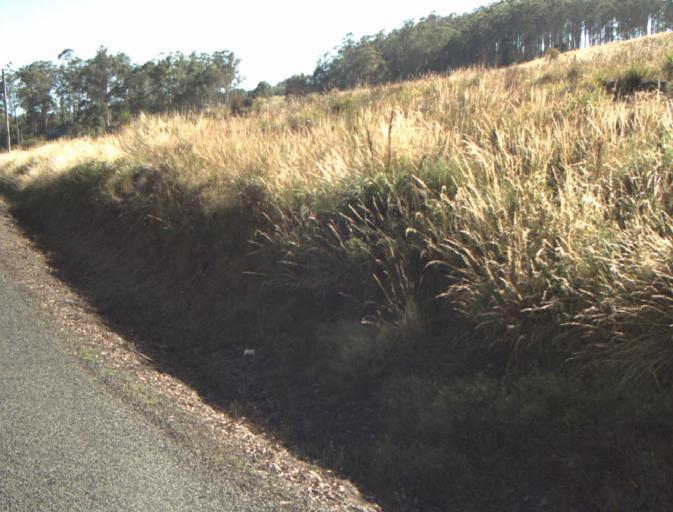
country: AU
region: Tasmania
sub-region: Launceston
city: Newstead
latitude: -41.3601
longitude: 147.3020
